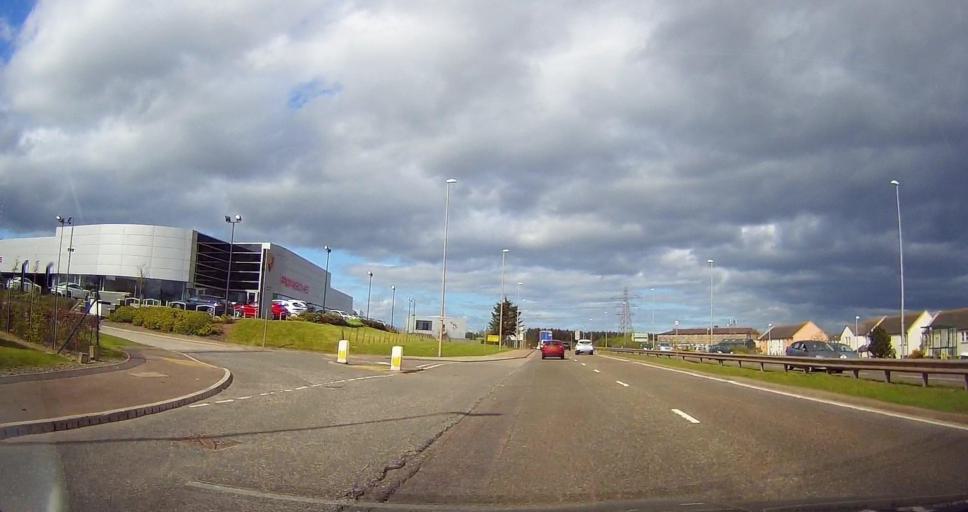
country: GB
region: Scotland
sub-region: Aberdeen City
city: Aberdeen
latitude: 57.1062
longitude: -2.0952
